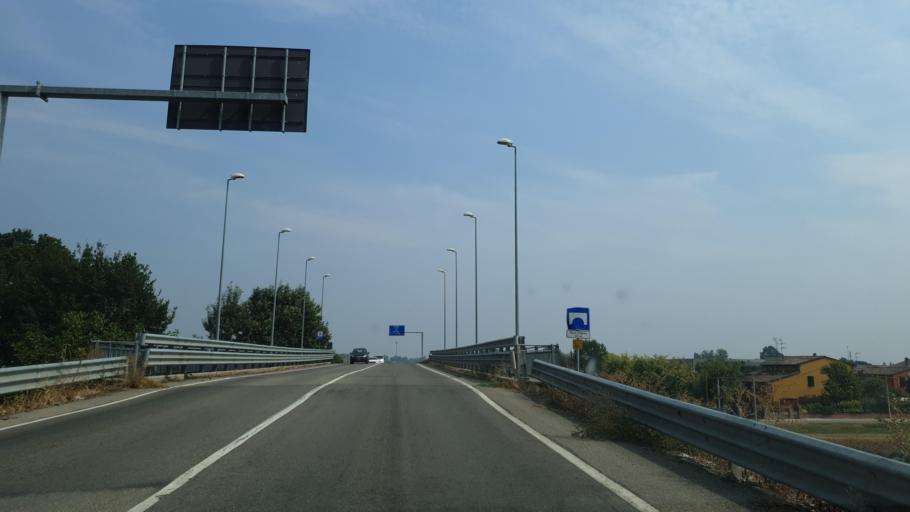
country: IT
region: Emilia-Romagna
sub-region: Provincia di Parma
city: San Secondo Parmense
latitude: 44.9284
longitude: 10.2304
